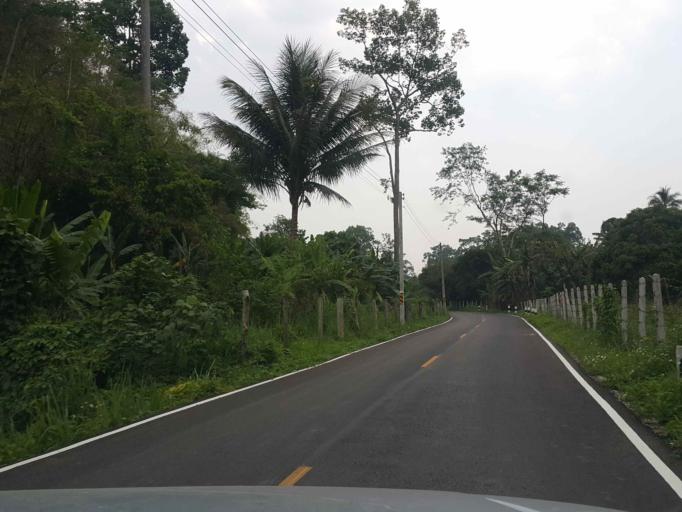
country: TH
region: Chiang Mai
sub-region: Amphoe Chiang Dao
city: Chiang Dao
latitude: 19.4083
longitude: 98.9238
